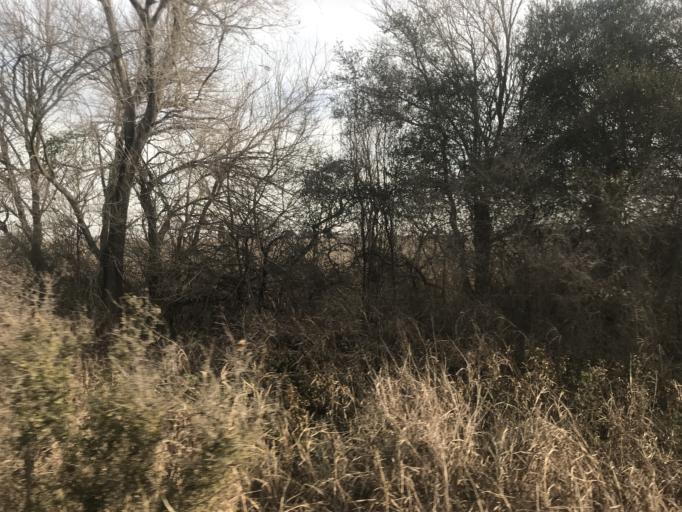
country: AR
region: Cordoba
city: Pilar
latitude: -31.7119
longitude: -63.8597
